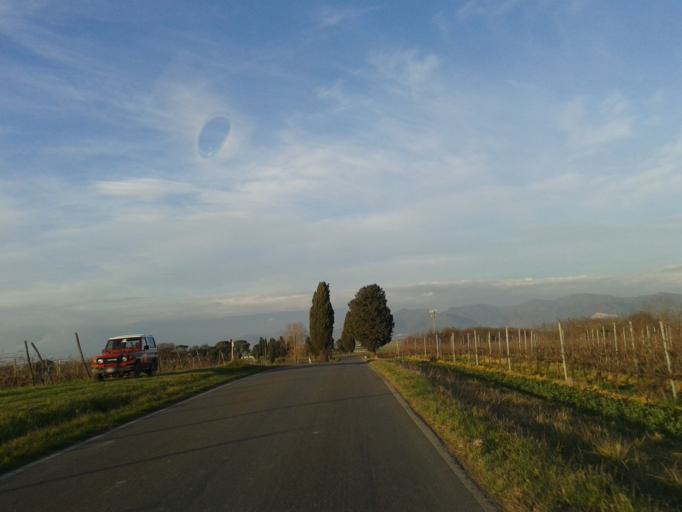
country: IT
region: Tuscany
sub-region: Provincia di Livorno
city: Vicarello
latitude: 43.5913
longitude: 10.4457
